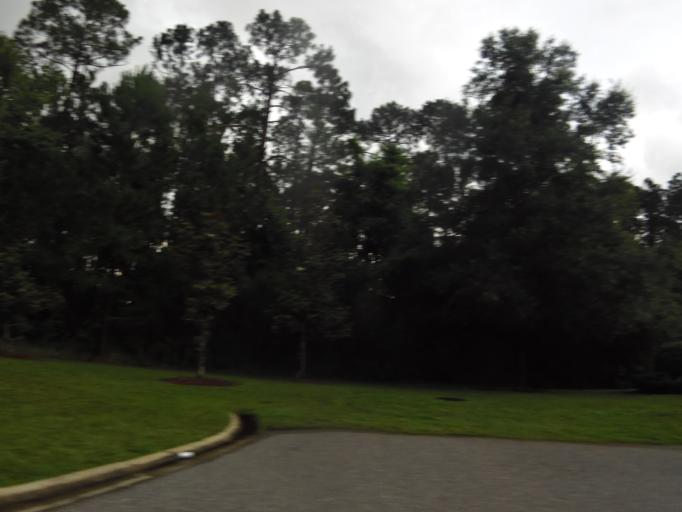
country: US
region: Florida
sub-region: Duval County
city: Jacksonville
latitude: 30.4778
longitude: -81.6073
